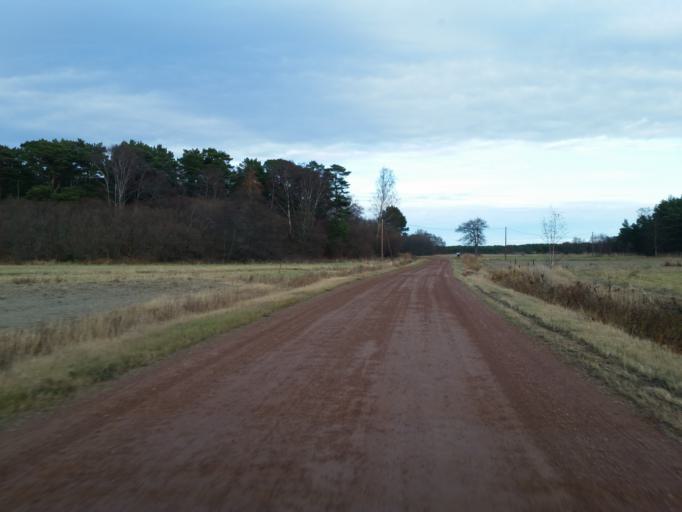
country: AX
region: Alands skaergard
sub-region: Kumlinge
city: Kumlinge
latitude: 60.2588
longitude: 20.8236
